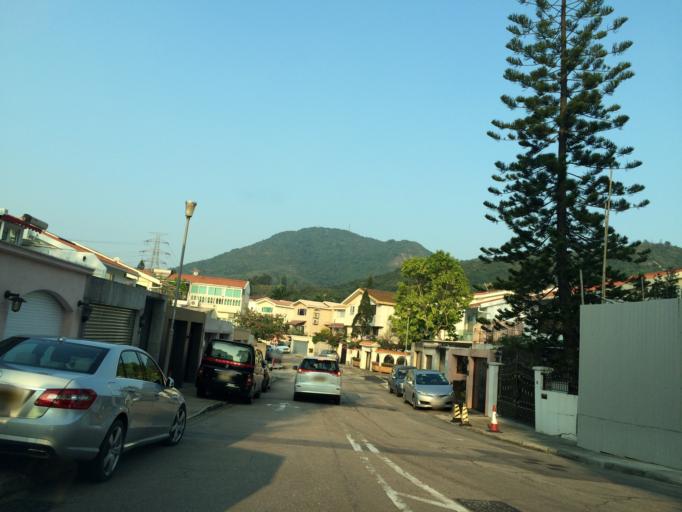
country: HK
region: Tai Po
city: Tai Po
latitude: 22.4633
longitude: 114.1542
